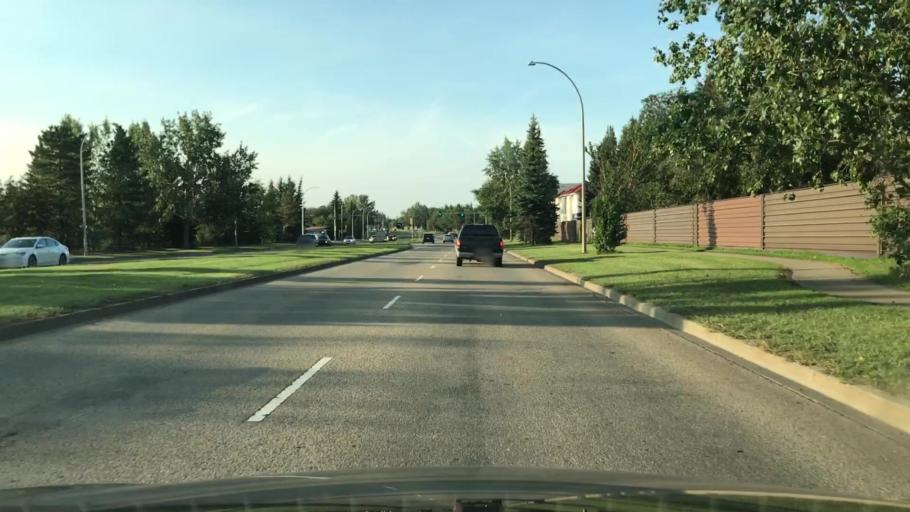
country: CA
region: Alberta
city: Beaumont
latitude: 53.4481
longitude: -113.4193
